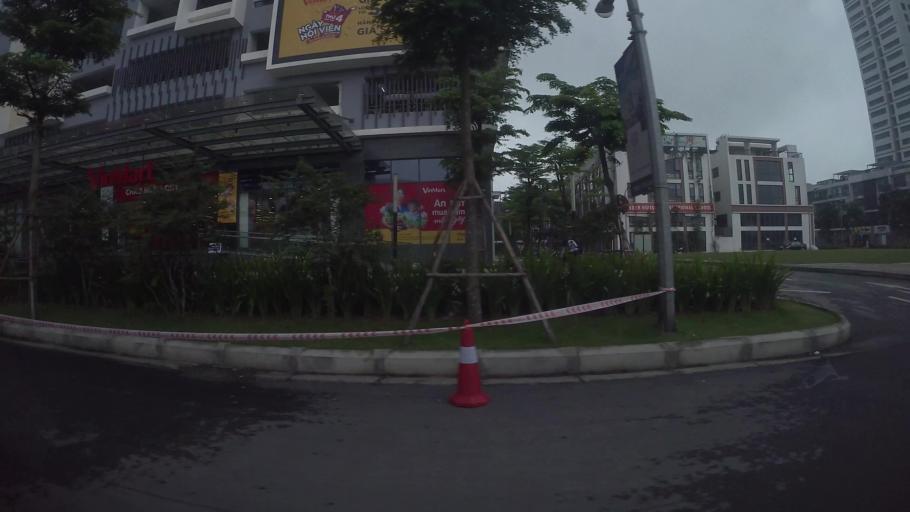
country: VN
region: Ha Noi
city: Van Dien
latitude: 20.9705
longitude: 105.8776
